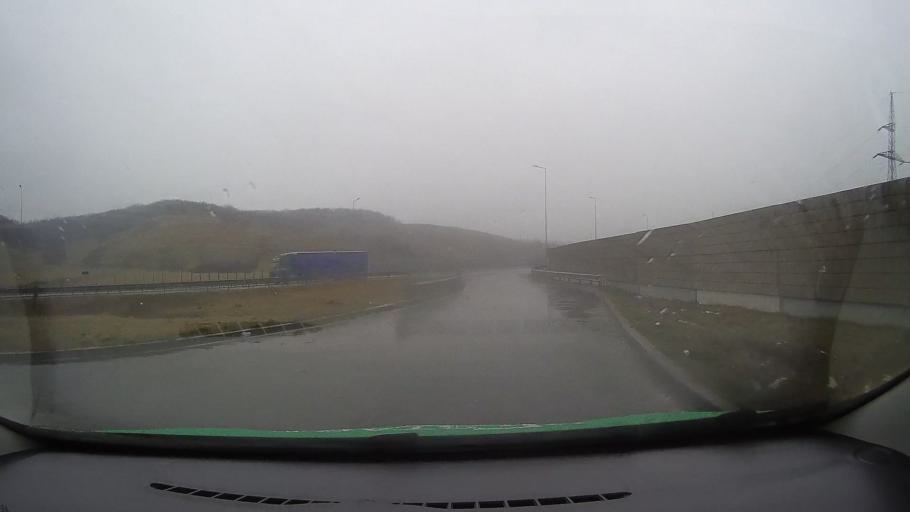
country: RO
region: Sibiu
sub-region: Comuna Cristian
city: Cristian
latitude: 45.7890
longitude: 24.0130
